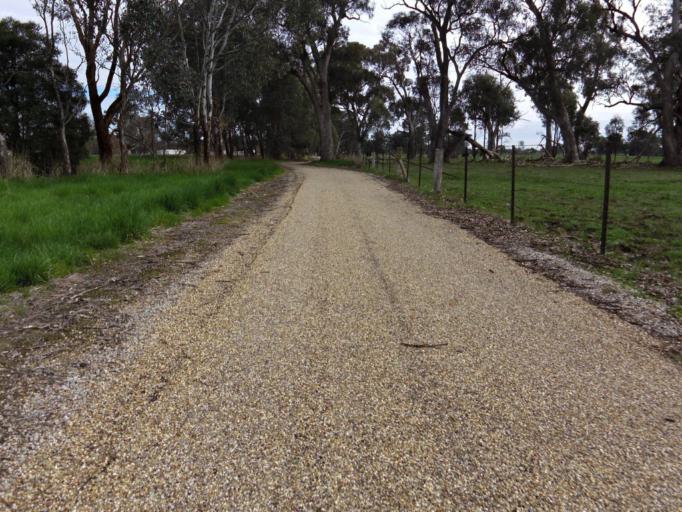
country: AU
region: Victoria
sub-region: Wangaratta
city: Wangaratta
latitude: -36.3922
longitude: 146.3378
